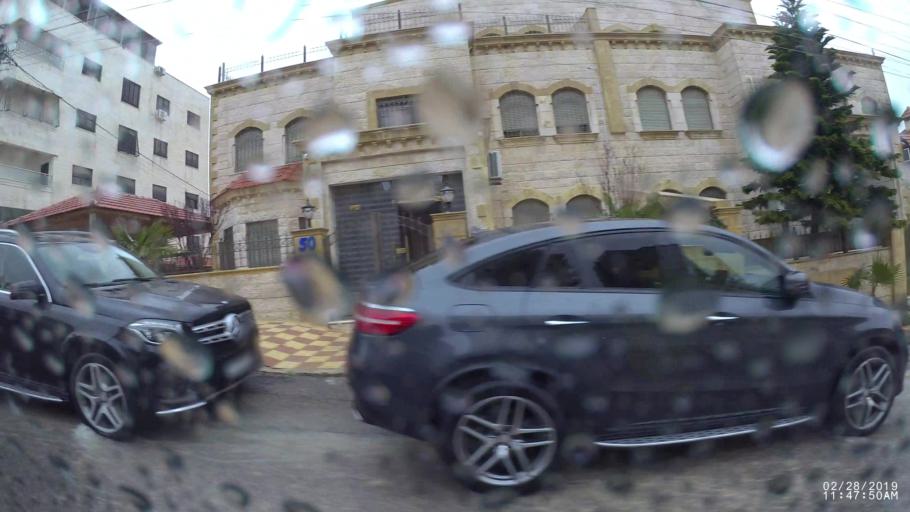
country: JO
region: Amman
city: Al Jubayhah
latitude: 32.0193
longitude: 35.8886
